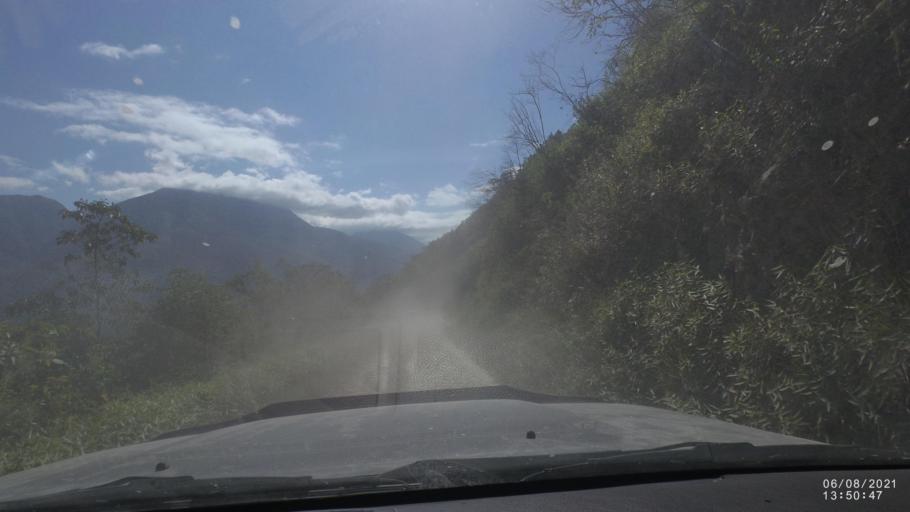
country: BO
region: La Paz
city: Quime
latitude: -16.6554
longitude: -66.7241
